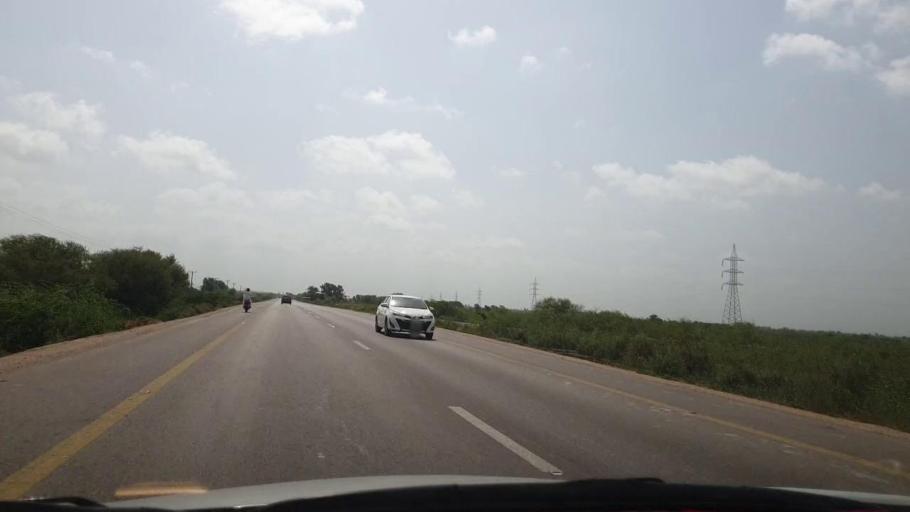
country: PK
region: Sindh
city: Talhar
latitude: 24.9226
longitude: 68.7212
